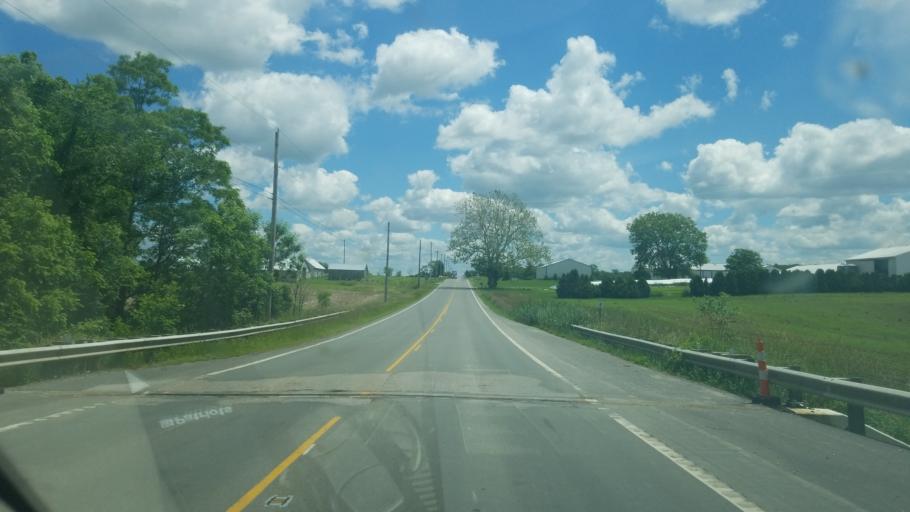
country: US
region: Ohio
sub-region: Huron County
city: New London
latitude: 41.0296
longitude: -82.3589
